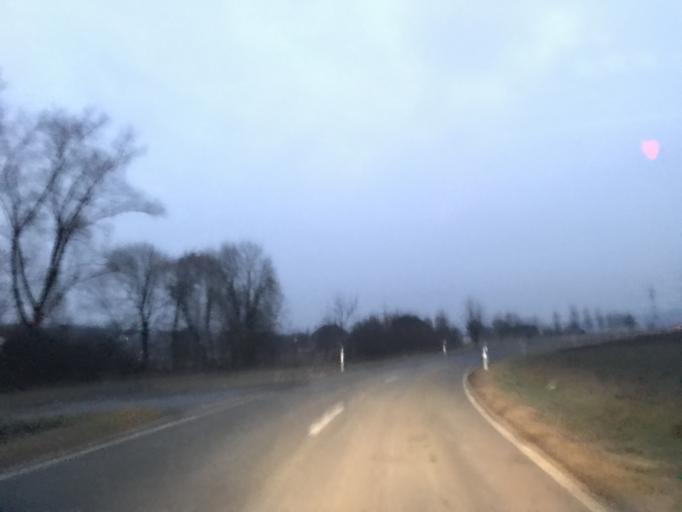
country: DE
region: Hesse
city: Trendelburg
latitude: 51.5471
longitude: 9.3799
